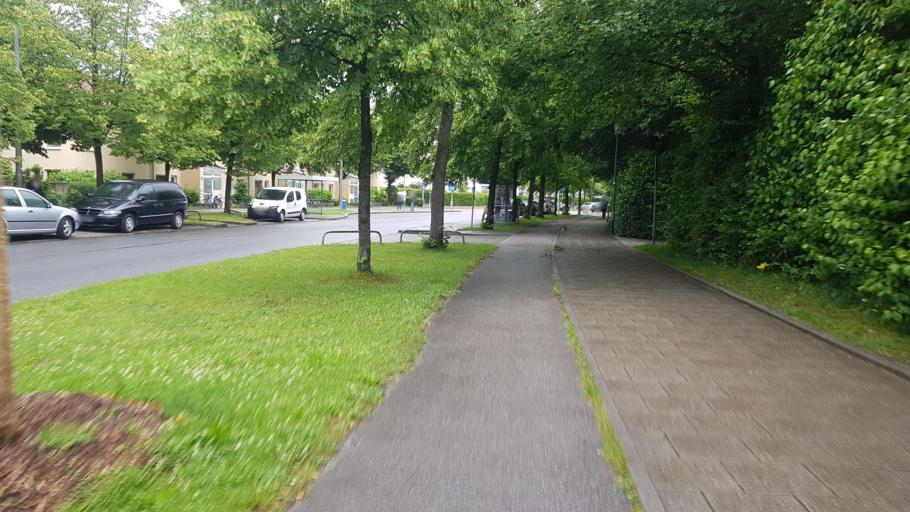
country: DE
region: Bavaria
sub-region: Upper Bavaria
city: Unterfoehring
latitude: 48.2048
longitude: 11.6000
